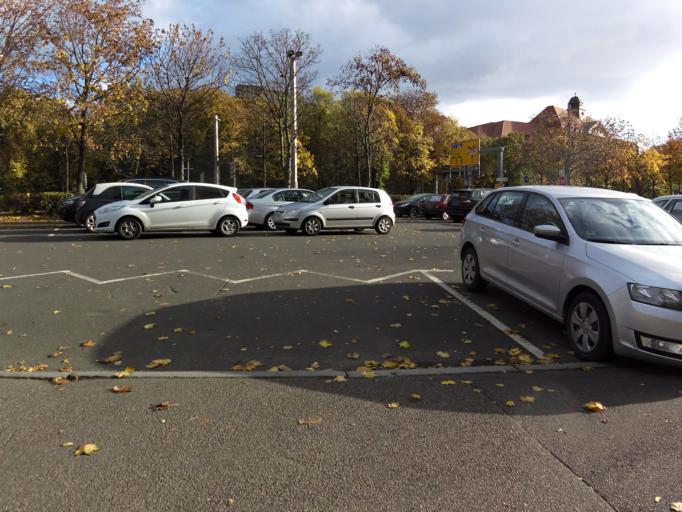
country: DE
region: Saxony
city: Leipzig
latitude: 51.3435
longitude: 12.3696
